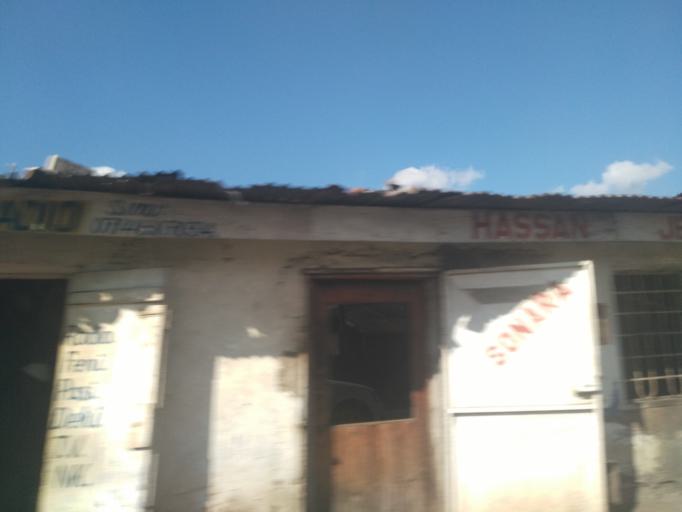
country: TZ
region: Dar es Salaam
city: Dar es Salaam
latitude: -6.8690
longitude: 39.2635
